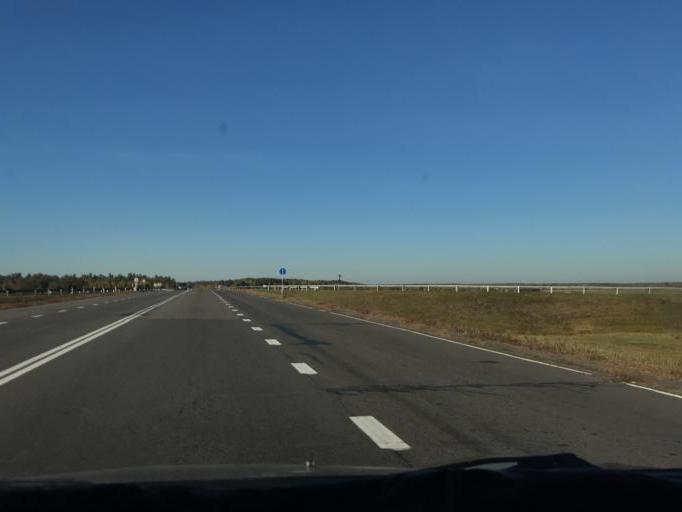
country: BY
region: Gomel
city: Kalinkavichy
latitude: 52.1236
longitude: 29.3764
